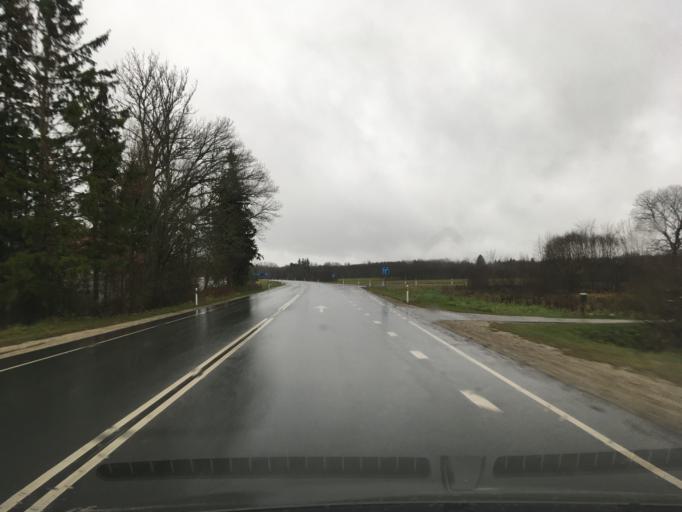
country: EE
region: Laeaene
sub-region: Lihula vald
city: Lihula
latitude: 58.8359
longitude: 24.0558
